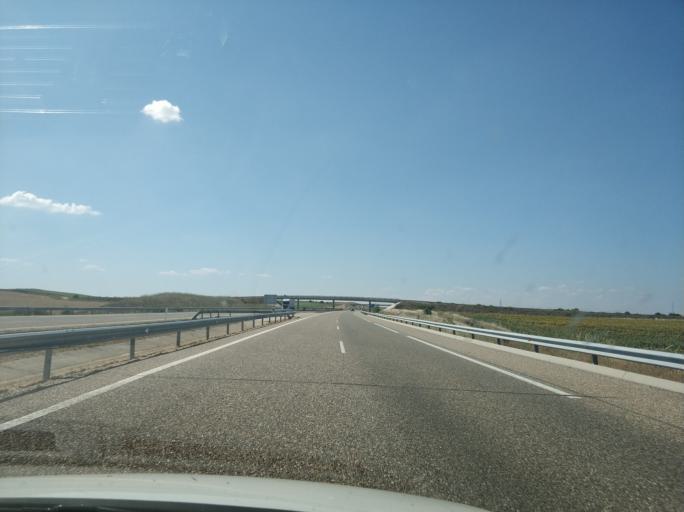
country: ES
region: Castille and Leon
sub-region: Provincia de Zamora
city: Roales
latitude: 41.5659
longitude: -5.7656
